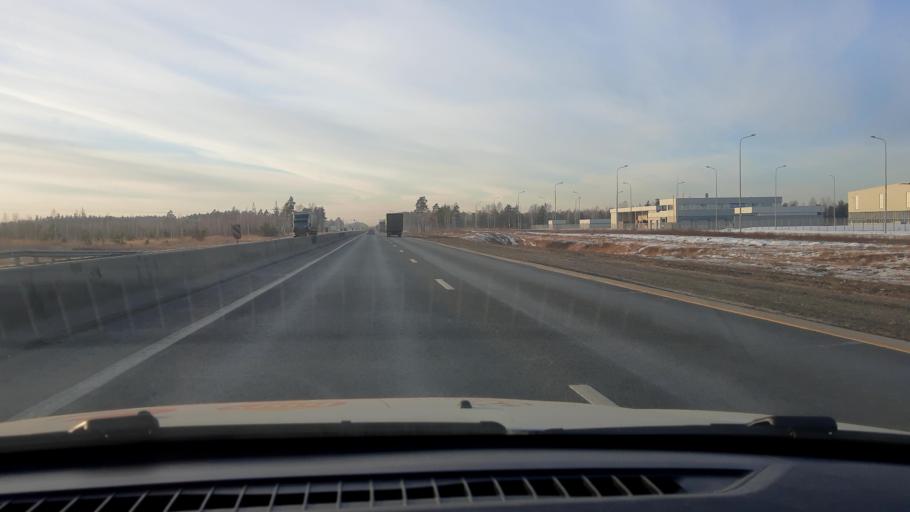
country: RU
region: Nizjnij Novgorod
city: Dzerzhinsk
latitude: 56.2972
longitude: 43.4377
